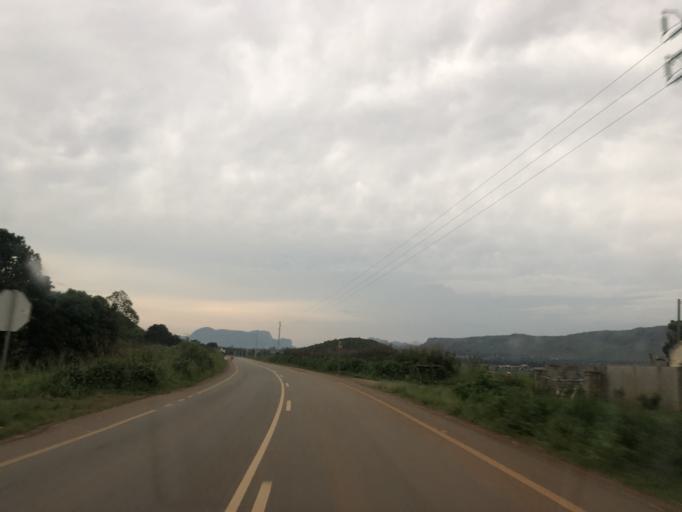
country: AO
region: Cuanza Sul
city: Uacu Cungo
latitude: -11.3252
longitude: 15.0900
